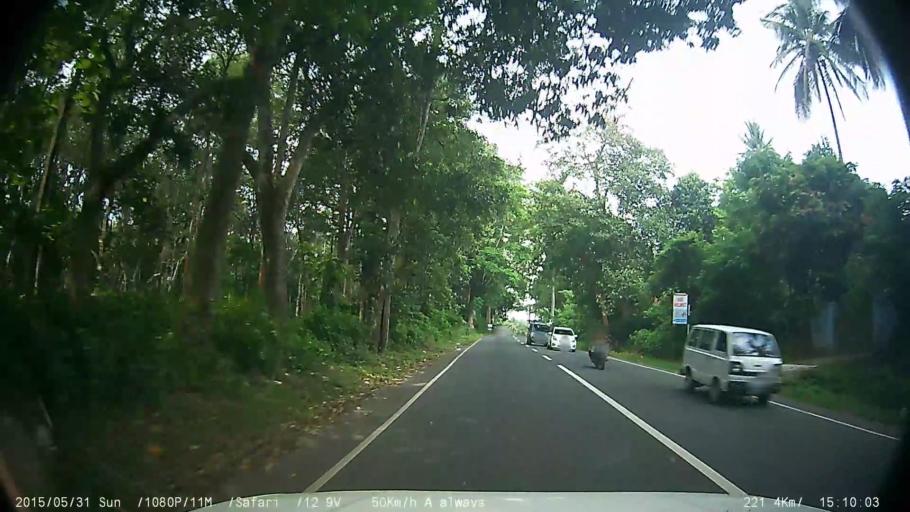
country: IN
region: Kerala
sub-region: Wayanad
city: Panamaram
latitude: 11.6548
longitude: 76.2232
